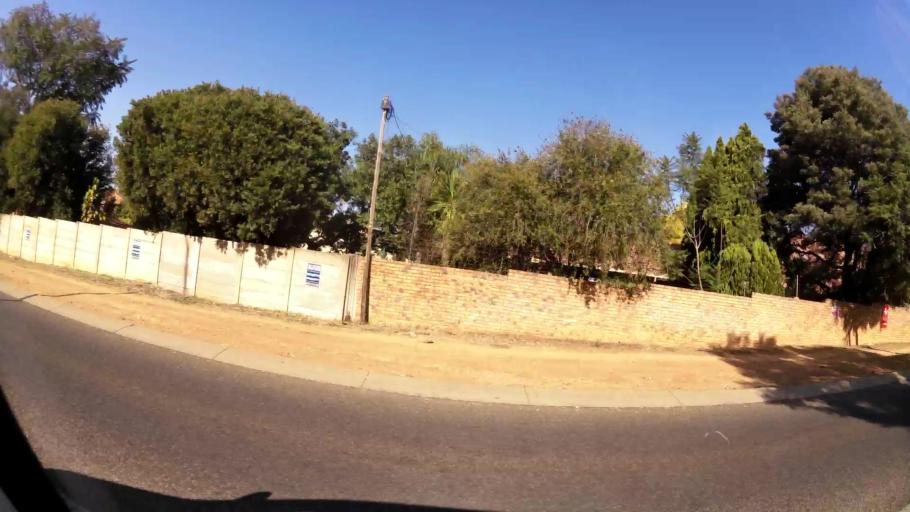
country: ZA
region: Gauteng
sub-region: City of Tshwane Metropolitan Municipality
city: Centurion
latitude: -25.8335
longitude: 28.2899
